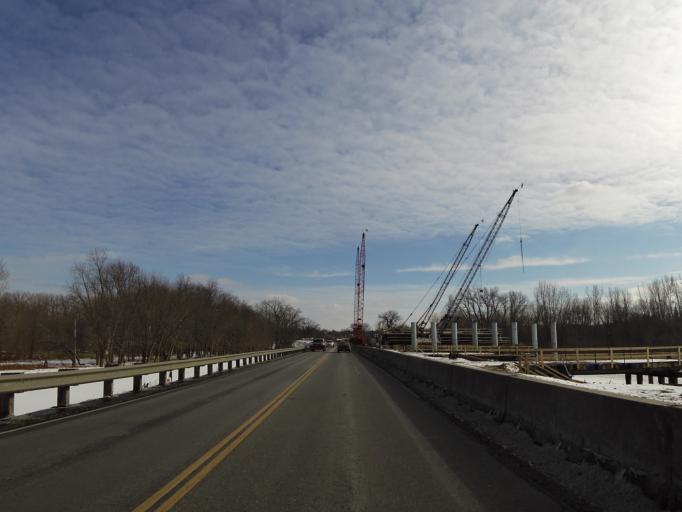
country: US
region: Minnesota
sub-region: Scott County
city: Shakopee
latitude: 44.8047
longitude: -93.5306
